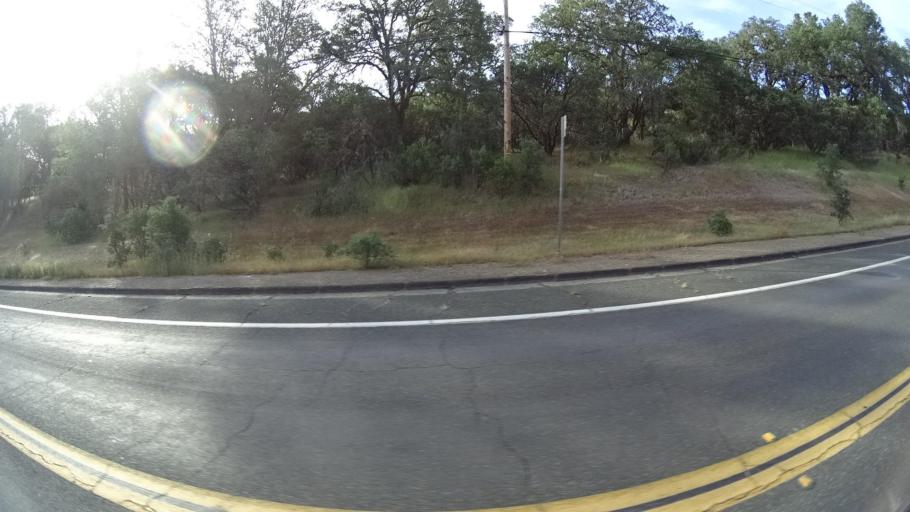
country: US
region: California
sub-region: Lake County
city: North Lakeport
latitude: 39.1158
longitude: -122.9047
